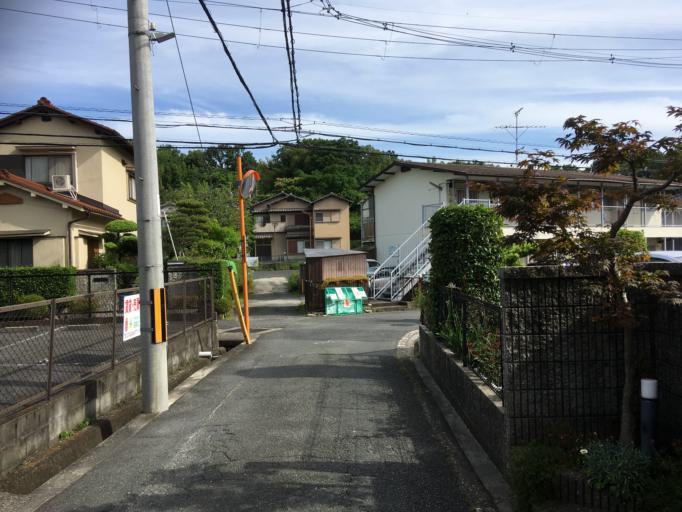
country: JP
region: Nara
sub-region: Ikoma-shi
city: Ikoma
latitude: 34.6978
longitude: 135.7387
